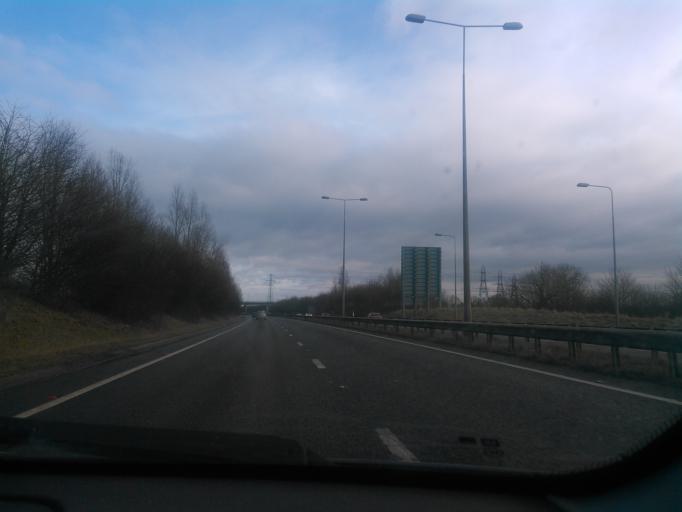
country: GB
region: England
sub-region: Derbyshire
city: Findern
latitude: 52.8657
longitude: -1.5524
